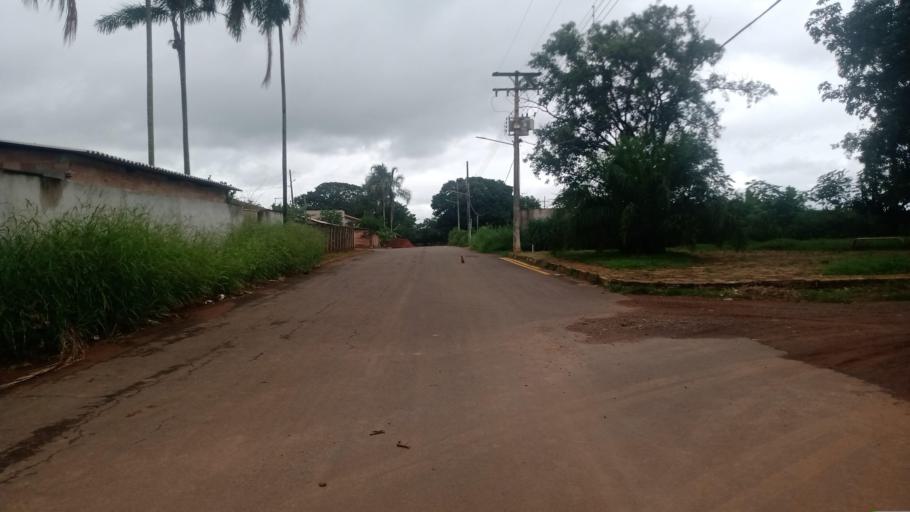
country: BR
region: Goias
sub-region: Senador Canedo
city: Senador Canedo
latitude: -16.7211
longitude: -49.1177
